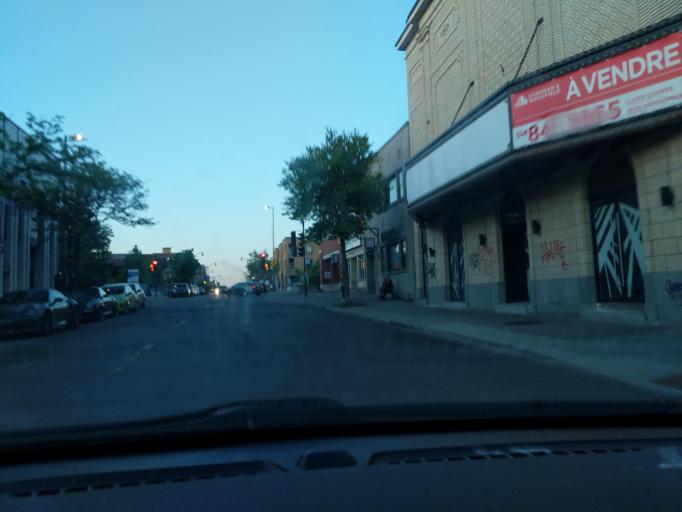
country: CA
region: Quebec
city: Westmount
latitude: 45.4779
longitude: -73.5842
